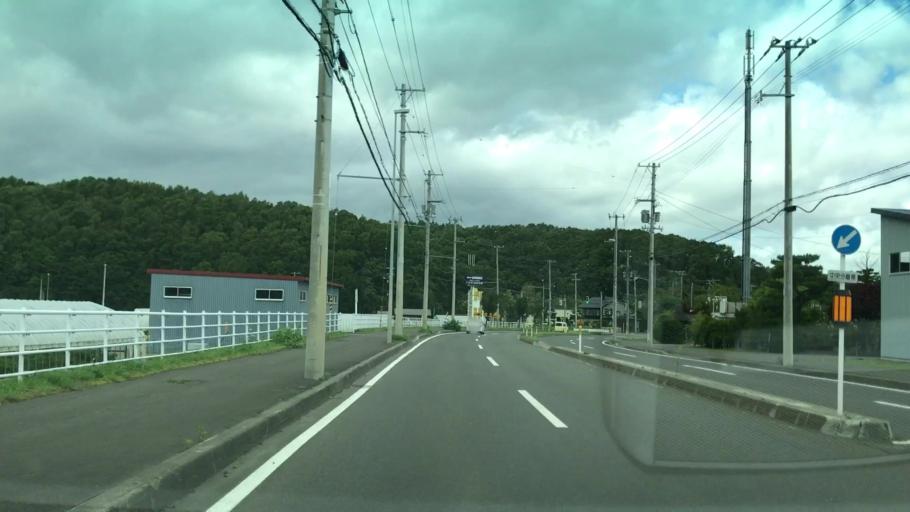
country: JP
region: Hokkaido
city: Kitahiroshima
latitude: 42.9785
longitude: 141.4412
